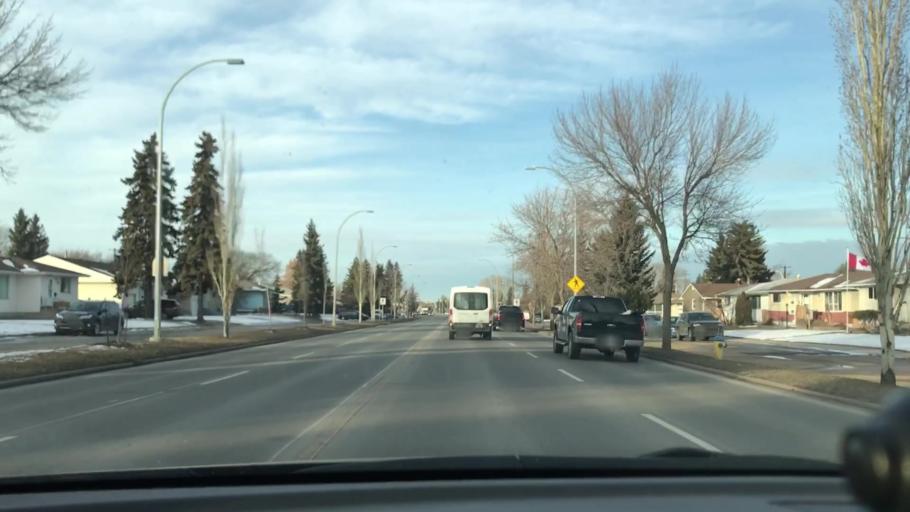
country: CA
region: Alberta
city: Edmonton
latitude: 53.5343
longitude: -113.4430
